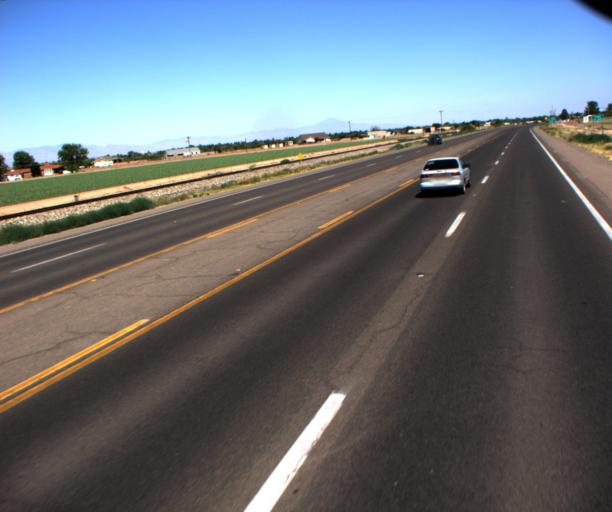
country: US
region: Arizona
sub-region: Graham County
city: Pima
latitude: 32.8847
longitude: -109.8115
